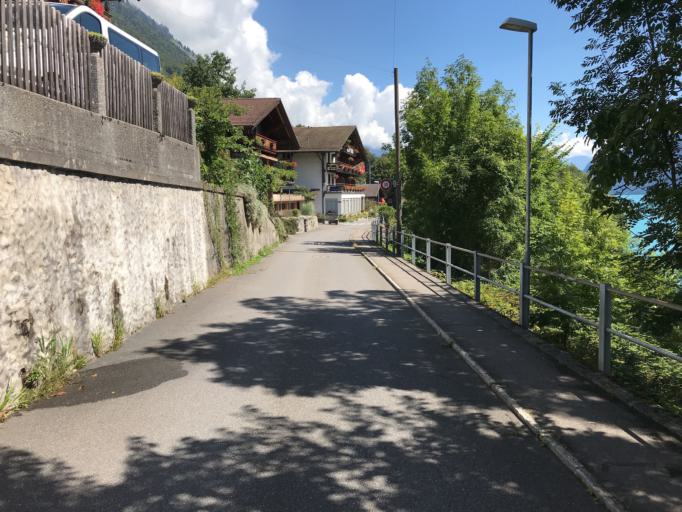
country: CH
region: Bern
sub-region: Interlaken-Oberhasli District
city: Ringgenberg
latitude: 46.7039
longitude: 7.9010
